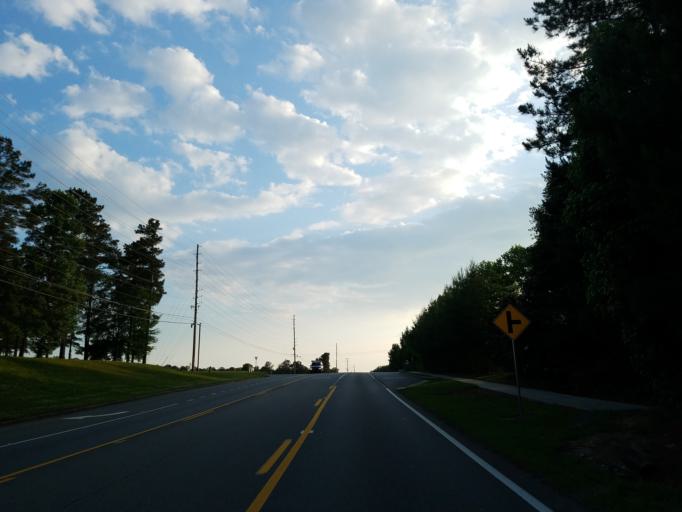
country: US
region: Georgia
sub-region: Cherokee County
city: Holly Springs
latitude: 34.1945
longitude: -84.5348
